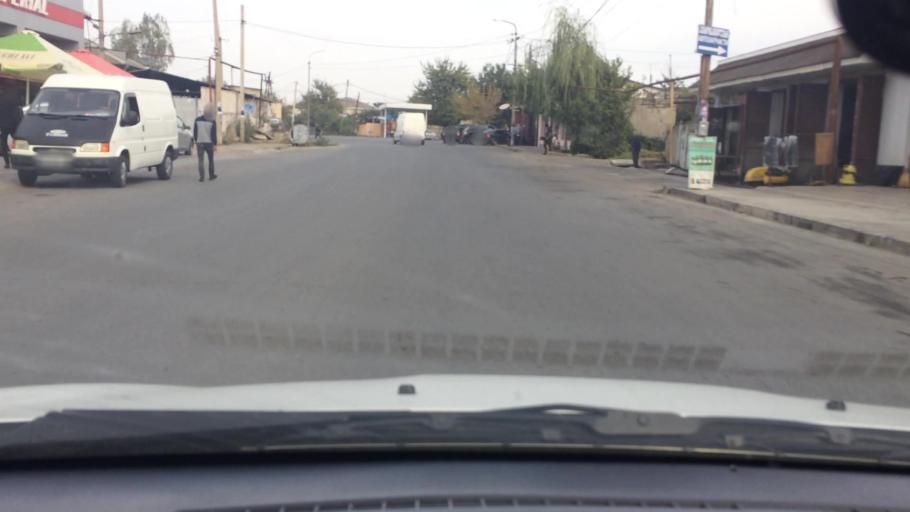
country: GE
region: Kvemo Kartli
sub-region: Marneuli
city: Marneuli
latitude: 41.4641
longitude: 44.8143
